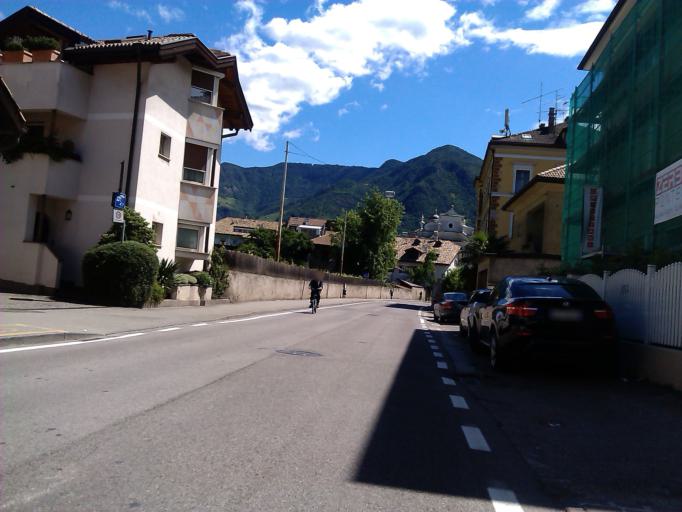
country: IT
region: Trentino-Alto Adige
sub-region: Bolzano
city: Bolzano
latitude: 46.5027
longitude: 11.3322
